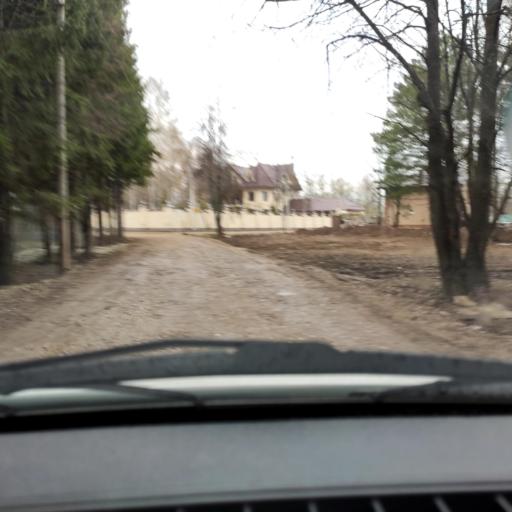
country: RU
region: Bashkortostan
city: Ufa
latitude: 54.7808
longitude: 56.1816
